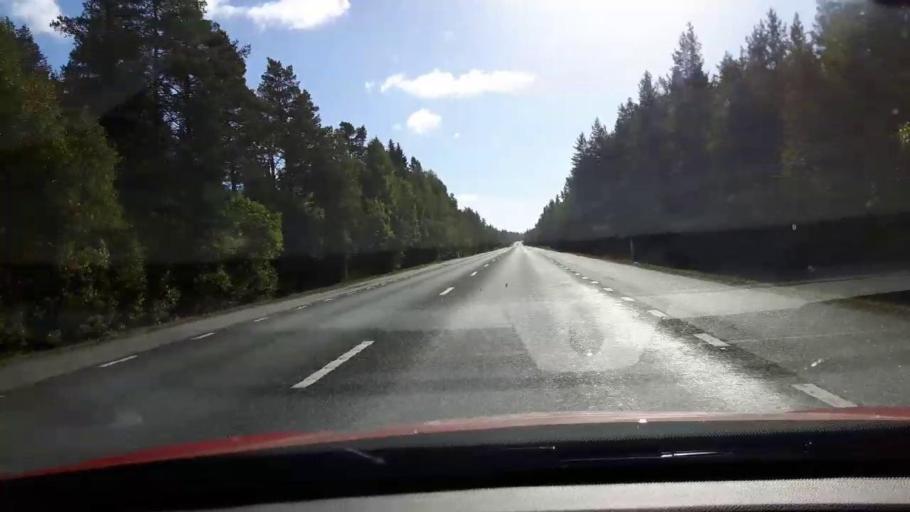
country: SE
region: Jaemtland
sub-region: Braecke Kommun
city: Braecke
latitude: 62.7111
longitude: 15.4764
